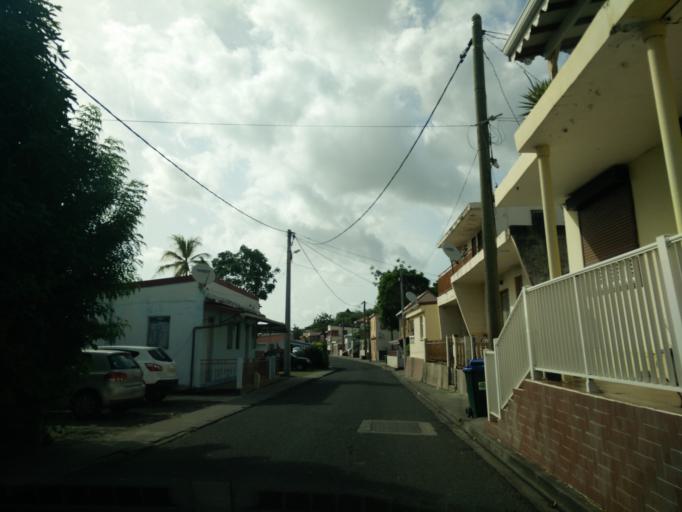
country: MQ
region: Martinique
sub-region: Martinique
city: Saint-Pierre
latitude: 14.7974
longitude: -61.2217
